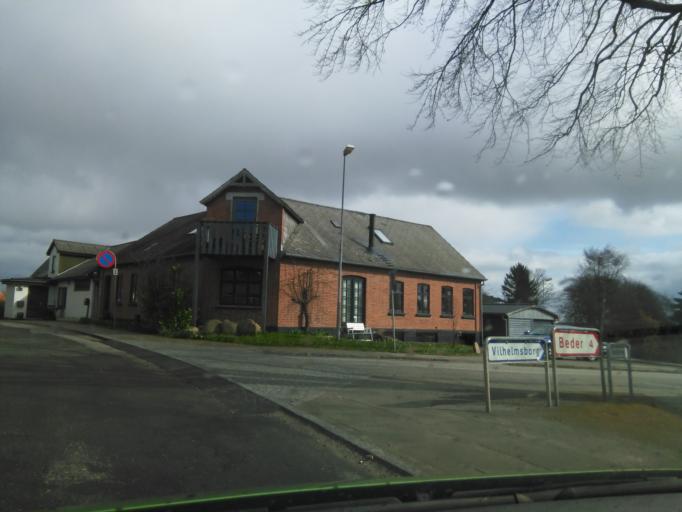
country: DK
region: Central Jutland
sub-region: Arhus Kommune
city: Marslet
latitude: 56.0652
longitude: 10.1602
